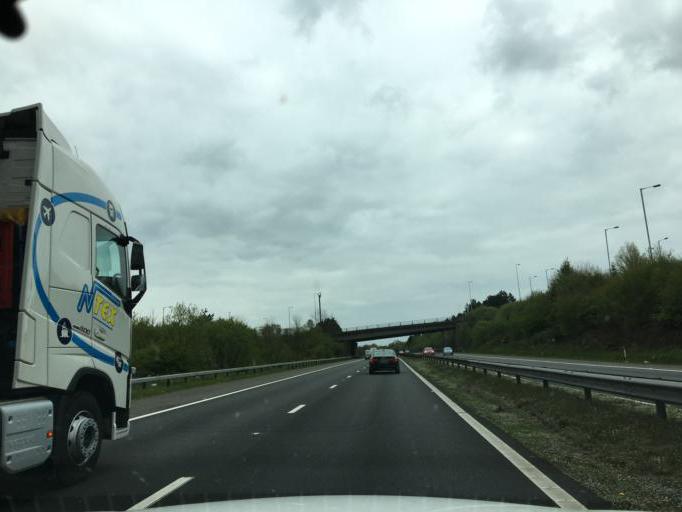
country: GB
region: Wales
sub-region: City and County of Swansea
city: Morriston
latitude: 51.6756
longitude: -3.9588
